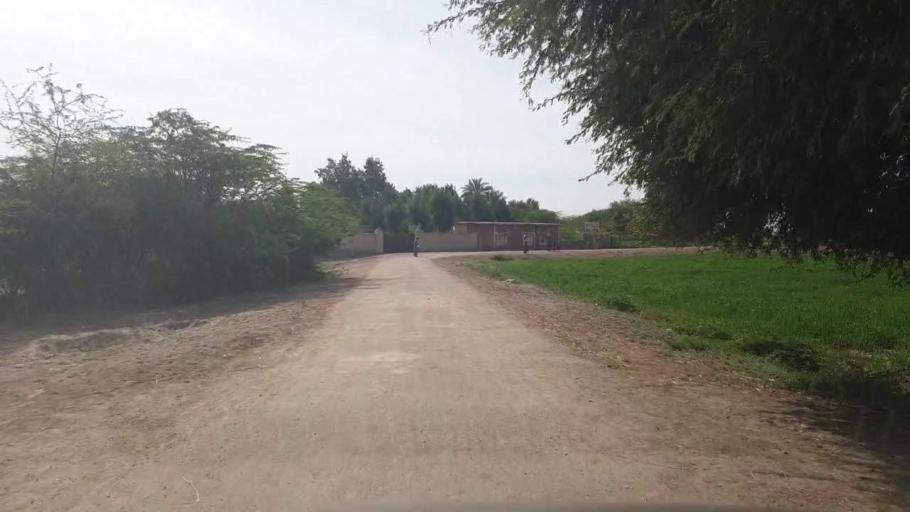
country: PK
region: Sindh
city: Umarkot
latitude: 25.3643
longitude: 69.6347
